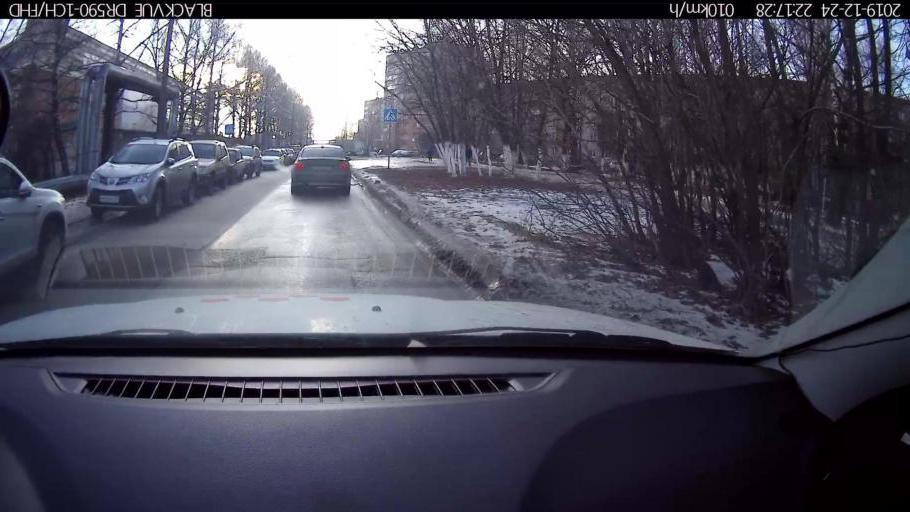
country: RU
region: Nizjnij Novgorod
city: Nizhniy Novgorod
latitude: 56.2418
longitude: 43.9725
